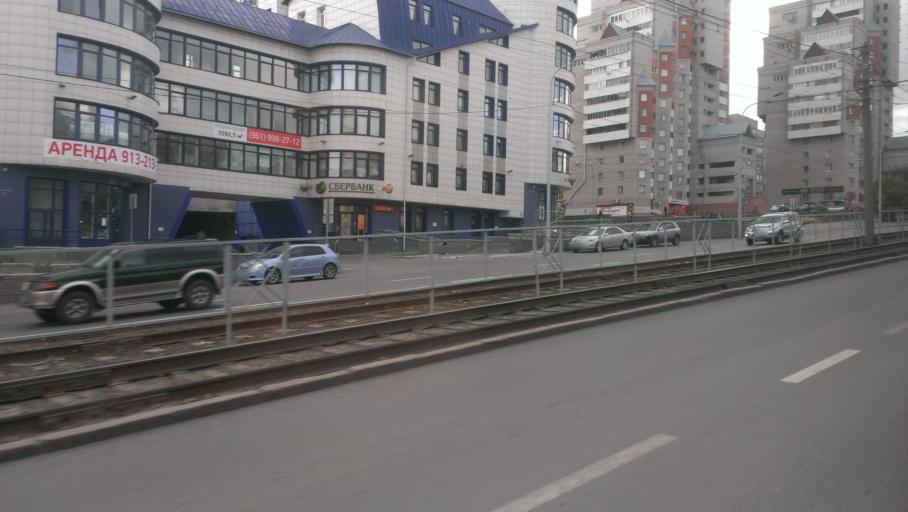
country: RU
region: Altai Krai
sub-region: Gorod Barnaulskiy
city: Barnaul
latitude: 53.3405
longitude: 83.7715
